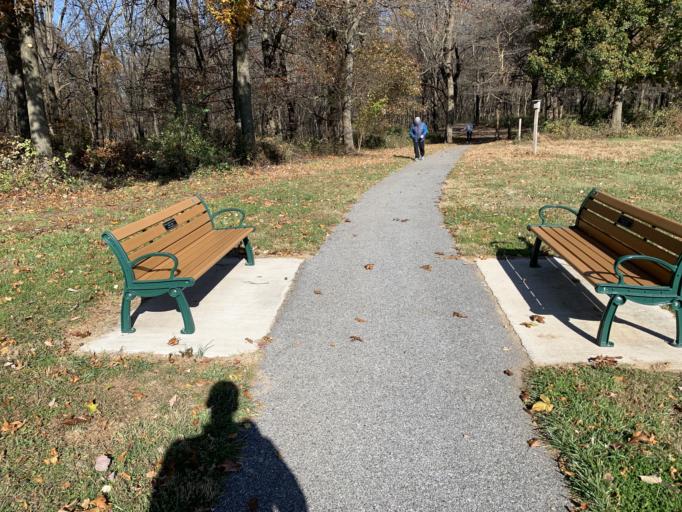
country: US
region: Maryland
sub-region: Carroll County
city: Hampstead
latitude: 39.6089
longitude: -76.8410
